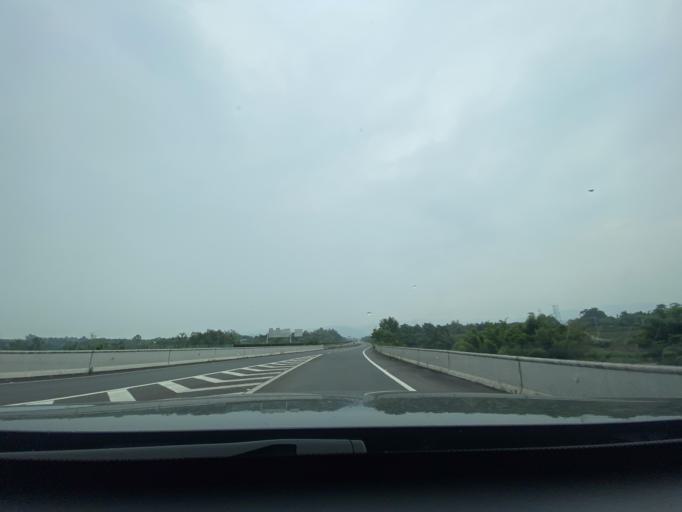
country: CN
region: Sichuan
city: Longquan
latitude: 30.3435
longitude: 104.1207
